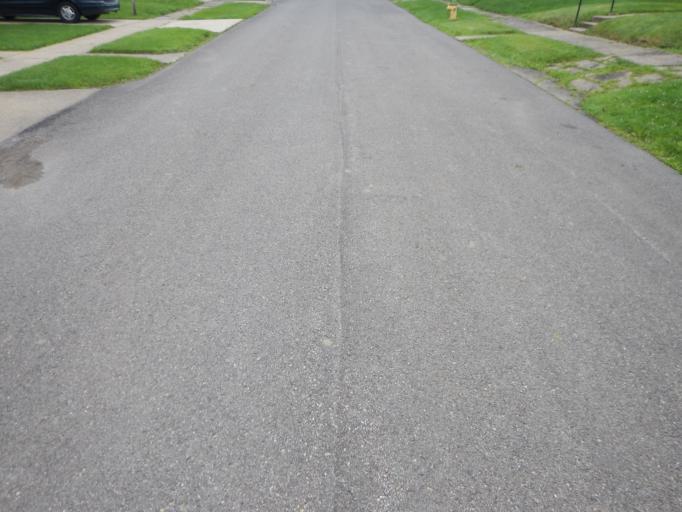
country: US
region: Ohio
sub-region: Muskingum County
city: North Zanesville
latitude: 39.9679
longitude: -82.0085
